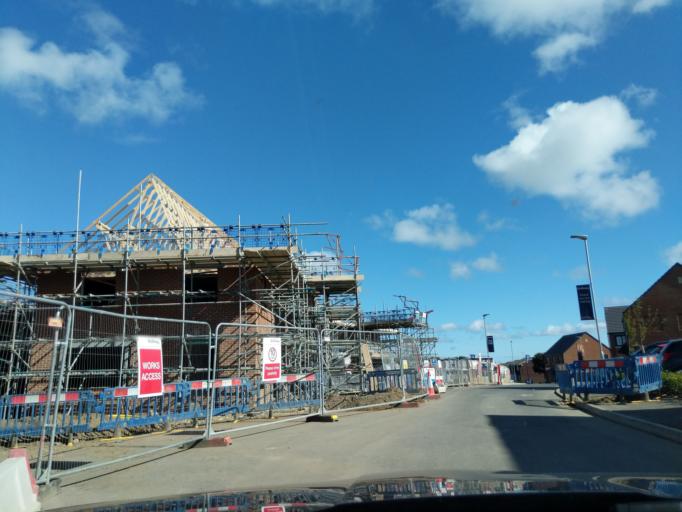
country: GB
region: England
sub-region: Northumberland
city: Newbiggin-by-the-Sea
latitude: 55.1701
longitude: -1.5457
